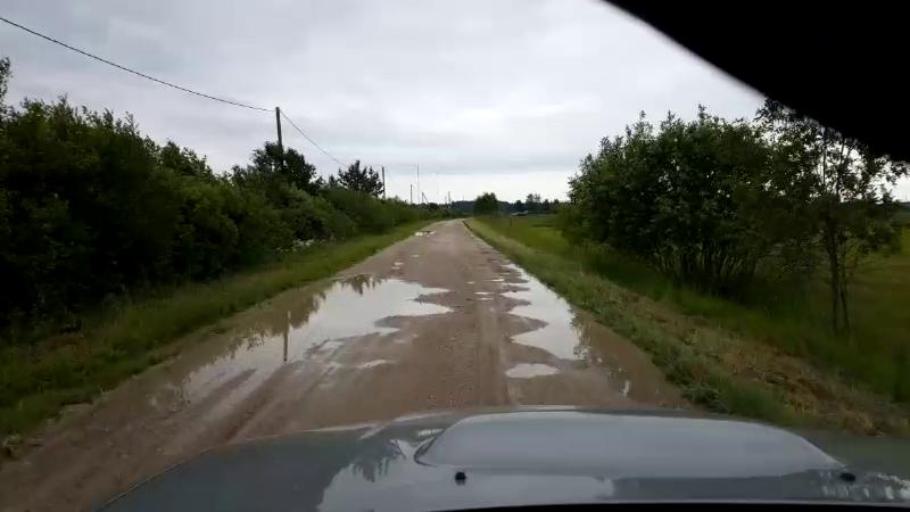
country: EE
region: Paernumaa
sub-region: Halinga vald
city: Parnu-Jaagupi
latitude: 58.5400
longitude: 24.5764
